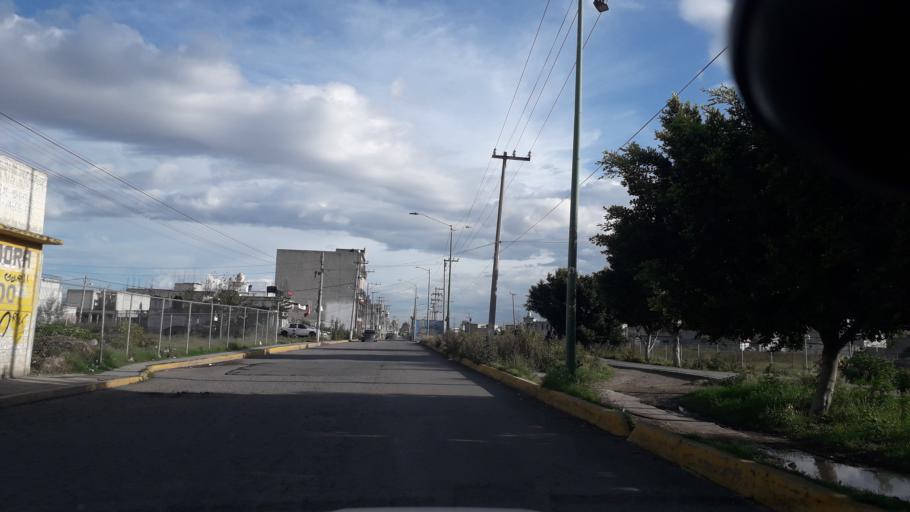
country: MX
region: Mexico
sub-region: Jaltenco
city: Alborada Jaltenco
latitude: 19.6658
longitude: -99.0742
